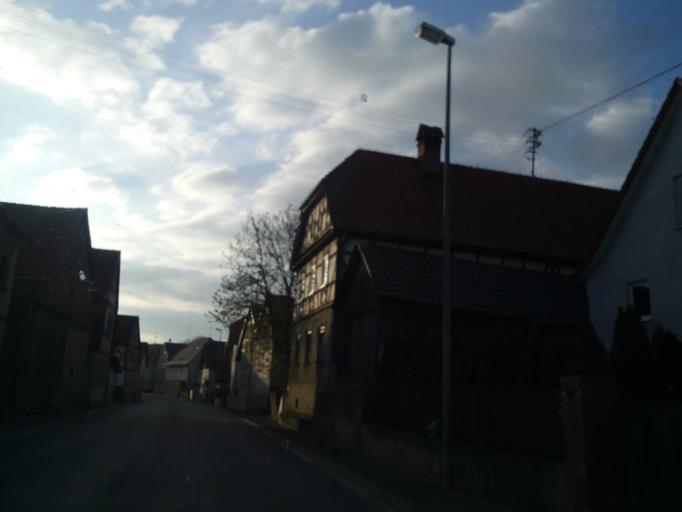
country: DE
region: Bavaria
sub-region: Regierungsbezirk Unterfranken
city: Maroldsweisach
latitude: 50.1848
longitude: 10.6704
